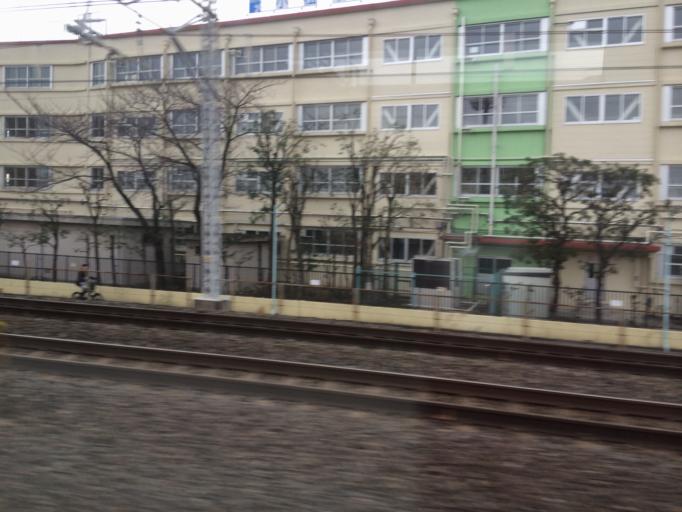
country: JP
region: Tokyo
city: Urayasu
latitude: 35.7207
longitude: 139.8642
